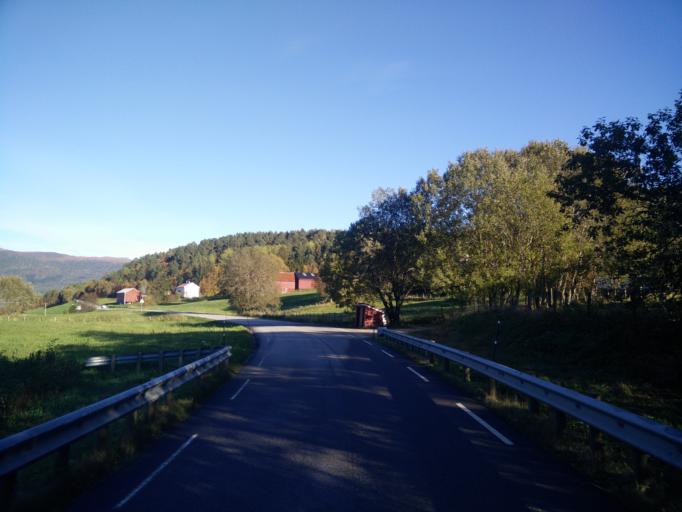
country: NO
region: More og Romsdal
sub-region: Halsa
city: Liaboen
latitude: 63.1335
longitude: 8.4052
